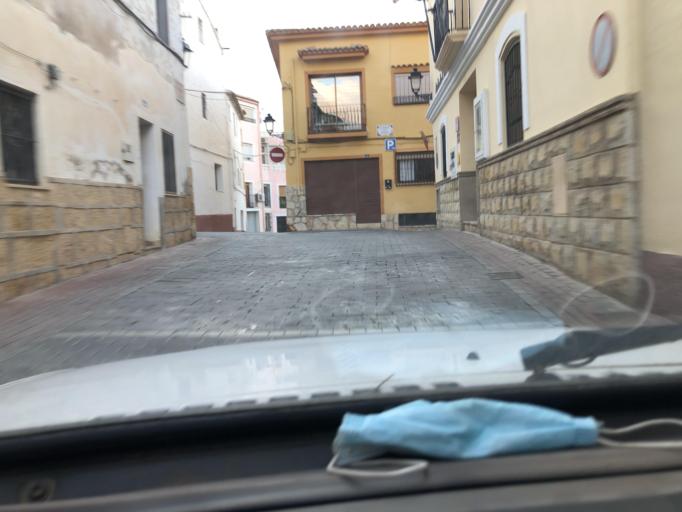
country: ES
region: Valencia
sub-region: Provincia de Alicante
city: Polop
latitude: 38.6218
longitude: -0.1273
